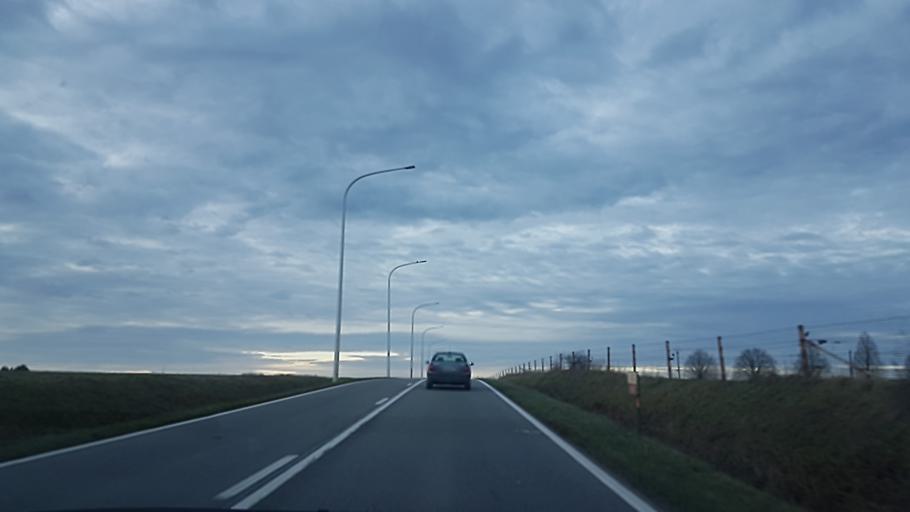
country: BE
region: Wallonia
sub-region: Province du Hainaut
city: Chimay
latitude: 50.0394
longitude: 4.3504
